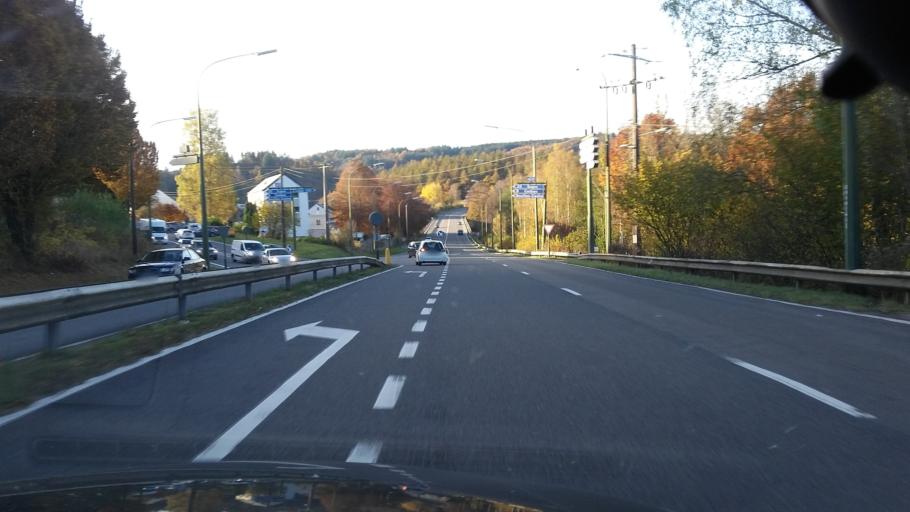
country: BE
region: Wallonia
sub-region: Province du Luxembourg
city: Bouillon
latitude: 49.7834
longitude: 5.0774
